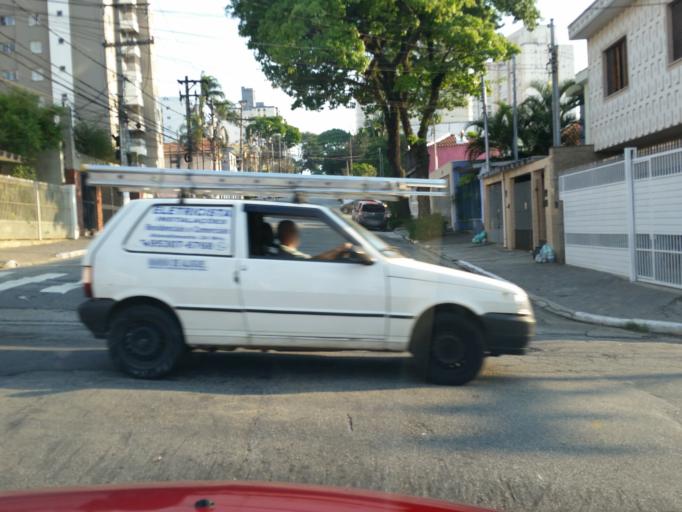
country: BR
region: Sao Paulo
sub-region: Sao Paulo
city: Sao Paulo
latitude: -23.6071
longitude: -46.6178
